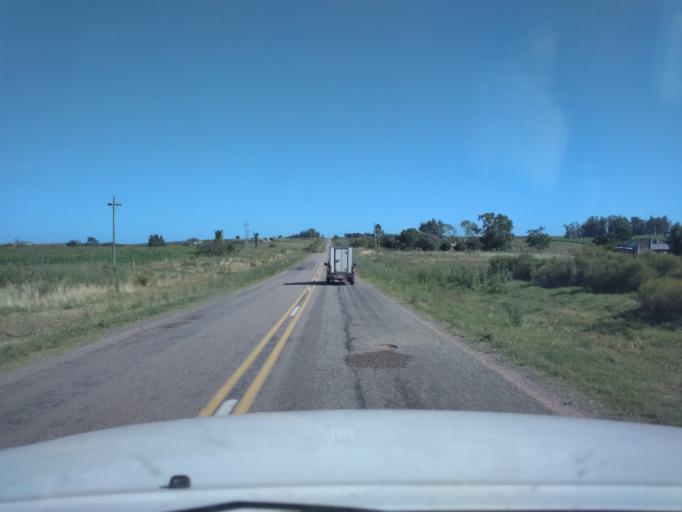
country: UY
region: Canelones
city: San Ramon
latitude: -34.1770
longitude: -55.9428
